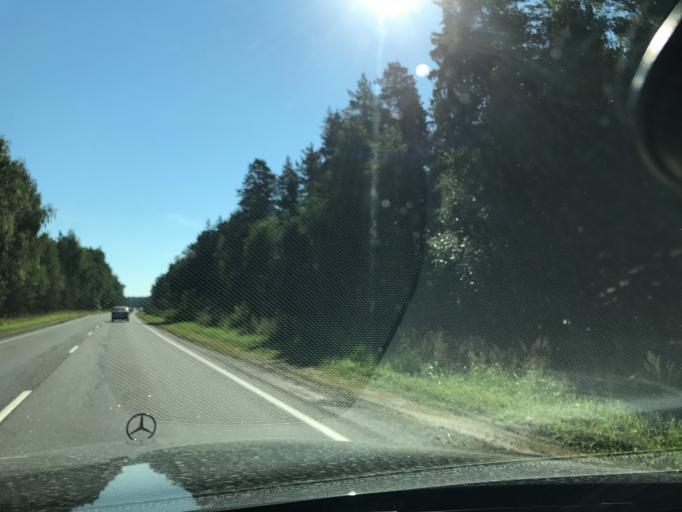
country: RU
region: Vladimir
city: Kirzhach
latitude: 56.1104
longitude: 38.7029
